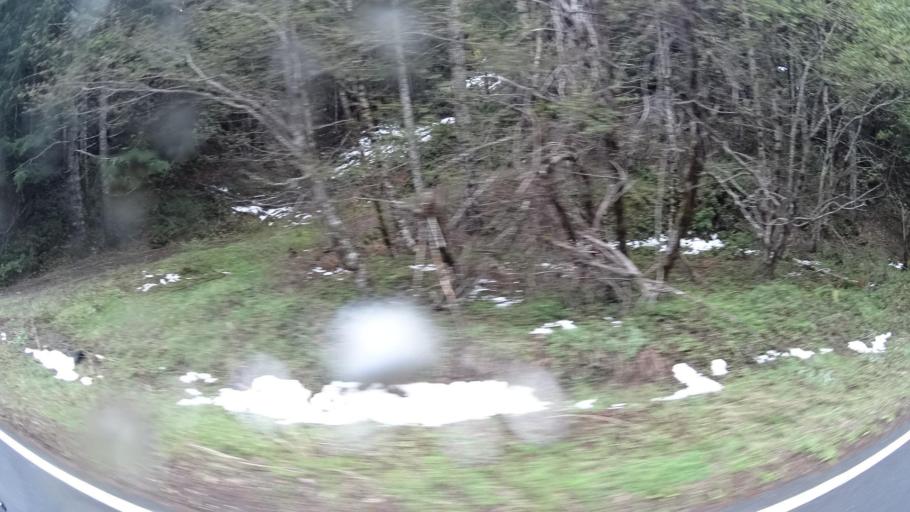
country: US
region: California
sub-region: Humboldt County
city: Willow Creek
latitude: 41.1552
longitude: -123.8186
